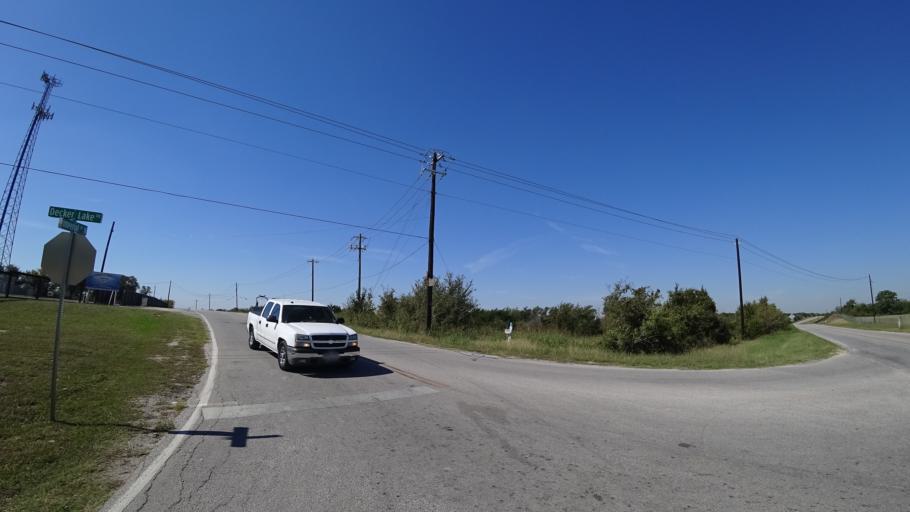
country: US
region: Texas
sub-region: Travis County
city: Hornsby Bend
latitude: 30.2850
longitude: -97.6183
